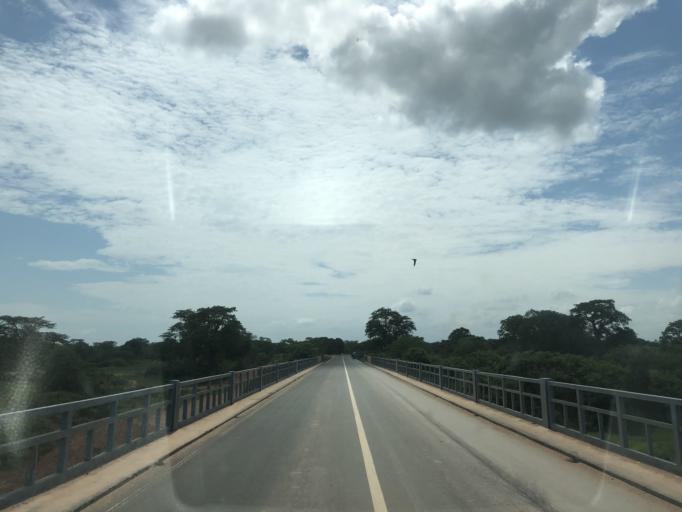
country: AO
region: Cuanza Norte
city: N'dalatando
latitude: -9.6659
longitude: 14.4249
